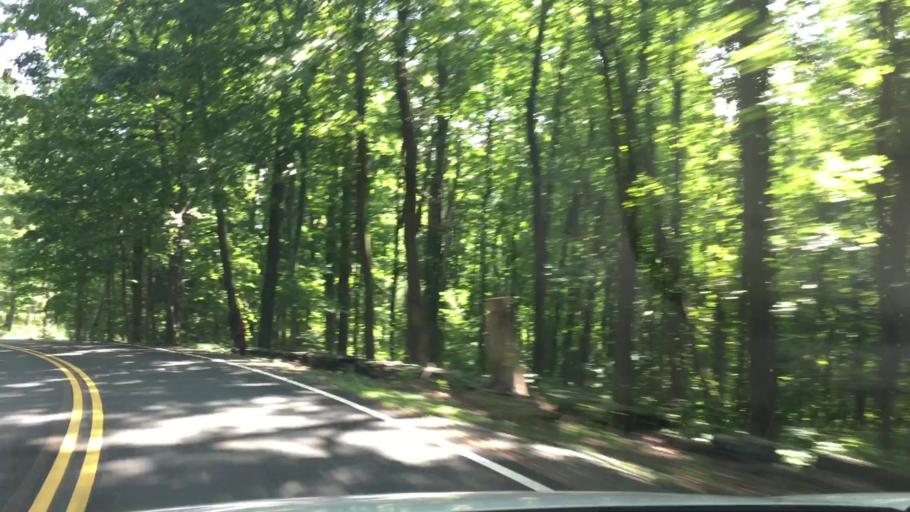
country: US
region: Massachusetts
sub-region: Berkshire County
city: Lenox
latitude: 42.3517
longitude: -73.3223
